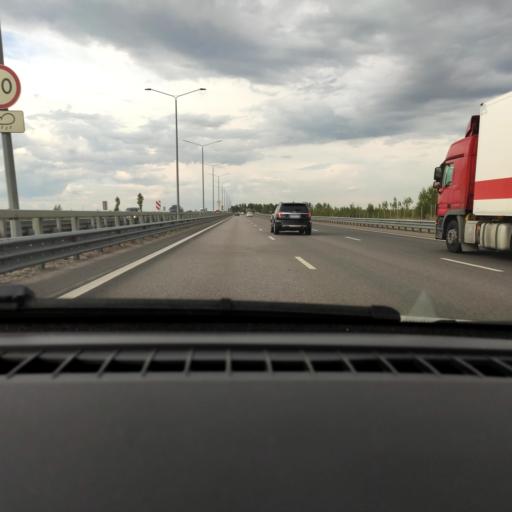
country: RU
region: Voronezj
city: Somovo
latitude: 51.7536
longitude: 39.3067
